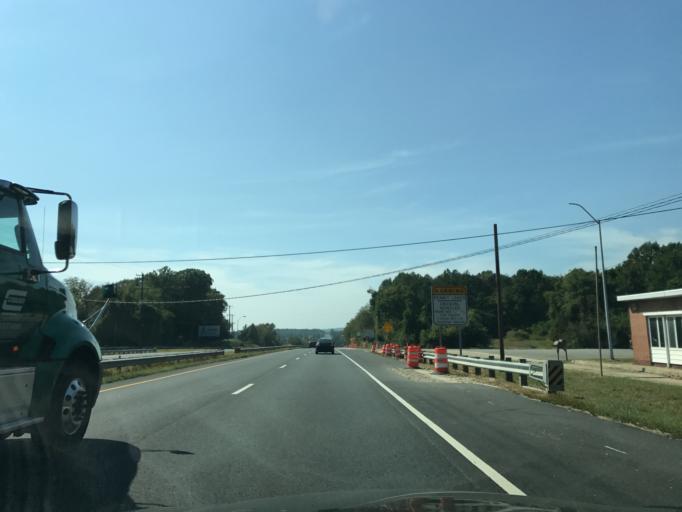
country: US
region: Maryland
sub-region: Cecil County
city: Charlestown
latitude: 39.5836
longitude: -76.0172
